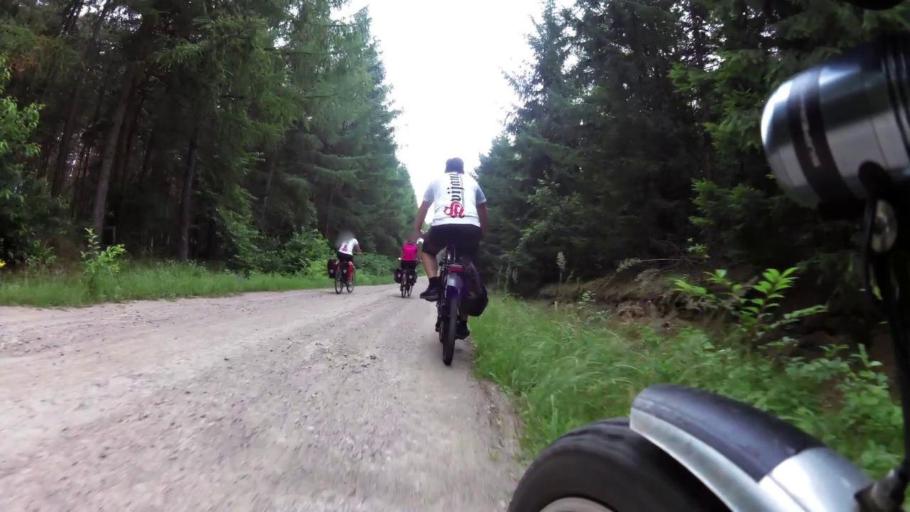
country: PL
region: West Pomeranian Voivodeship
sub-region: Powiat gryfinski
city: Mieszkowice
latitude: 52.8387
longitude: 14.5951
